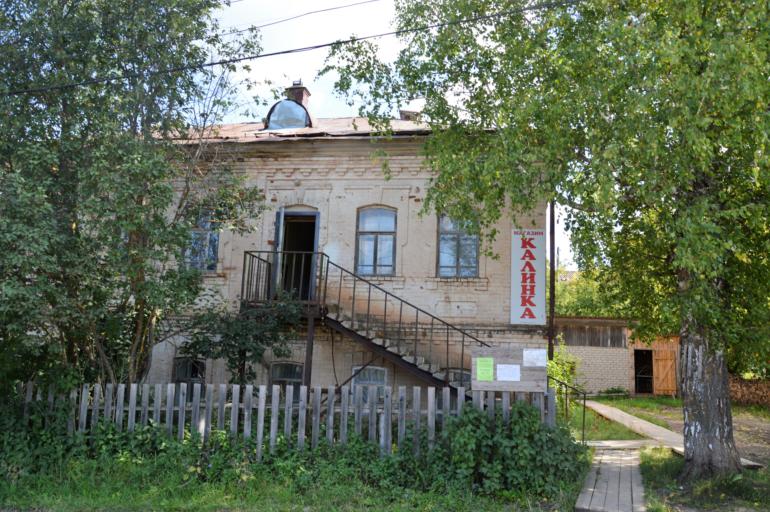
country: RU
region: Kirov
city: Nizhneivkino
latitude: 57.8131
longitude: 49.5675
